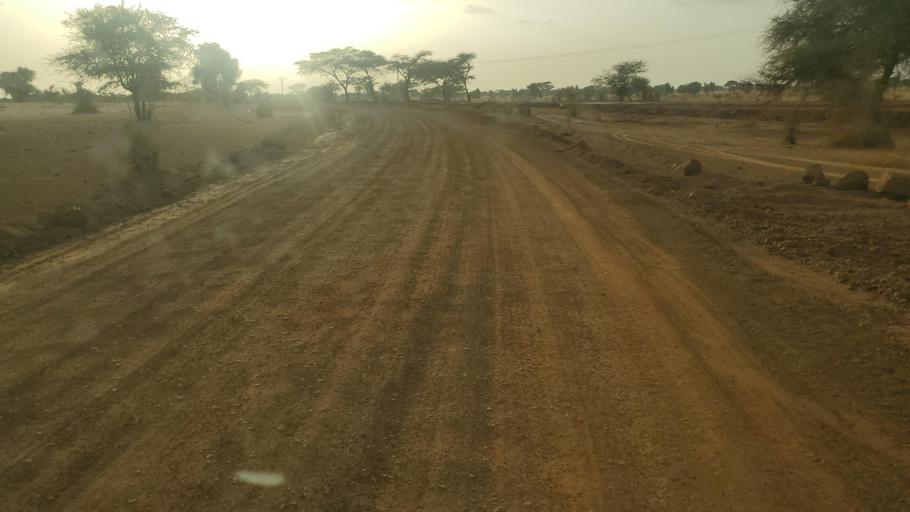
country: SN
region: Louga
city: Dara
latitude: 15.3648
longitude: -15.5573
